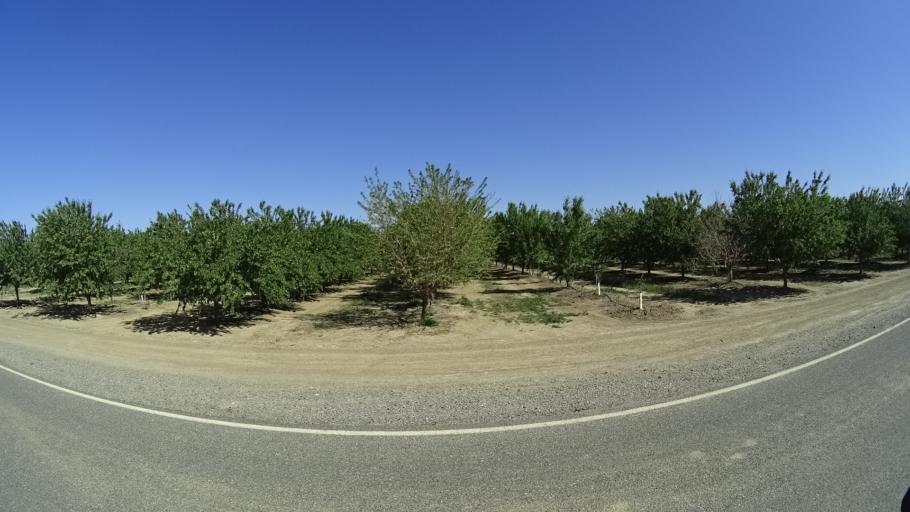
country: US
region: California
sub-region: Glenn County
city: Willows
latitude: 39.6238
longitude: -122.1442
